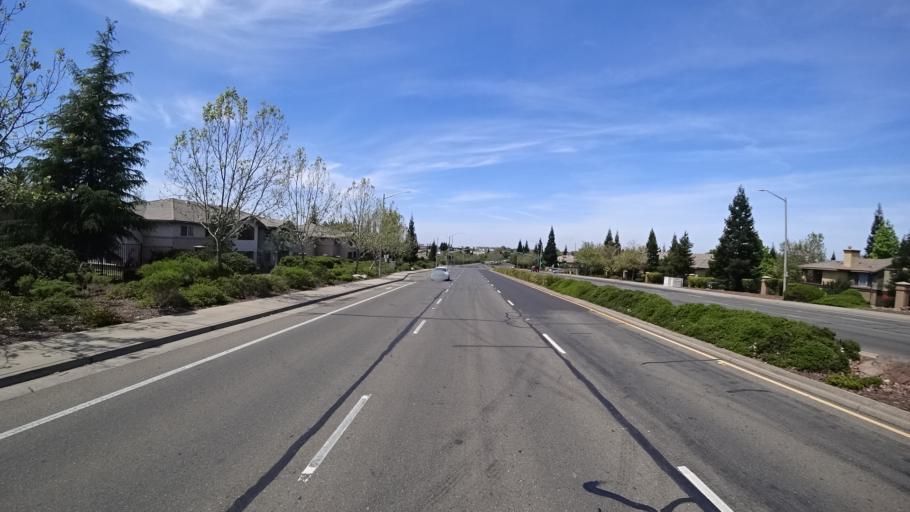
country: US
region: California
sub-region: Placer County
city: Rocklin
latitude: 38.8080
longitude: -121.2785
